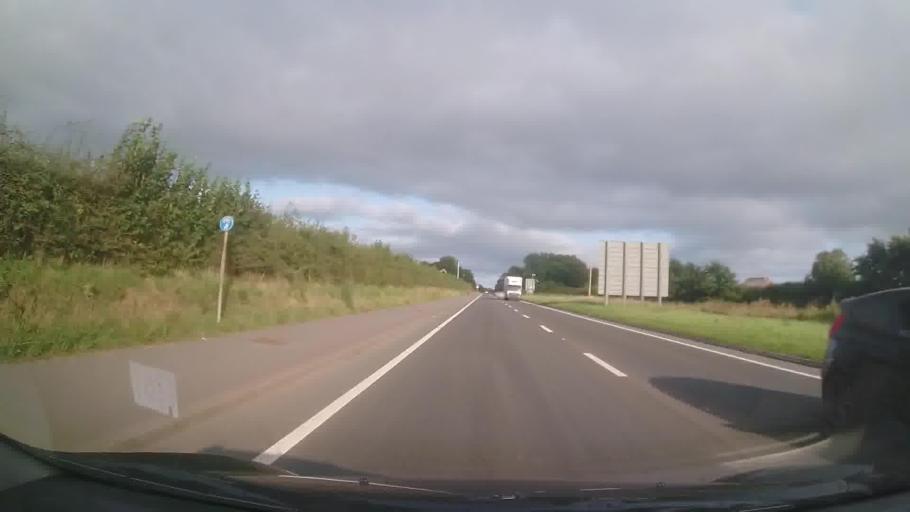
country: GB
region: Wales
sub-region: Pembrokeshire
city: Manorbier
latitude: 51.6931
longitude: -4.8261
